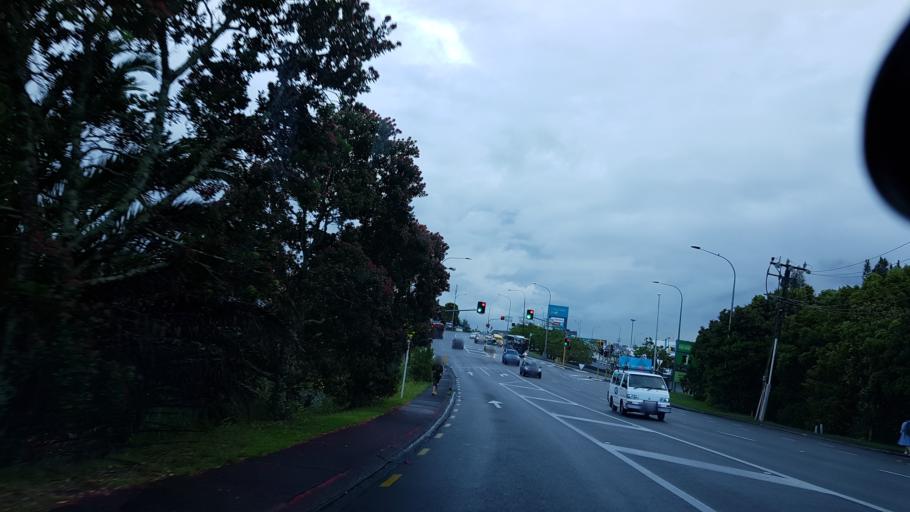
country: NZ
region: Auckland
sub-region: Auckland
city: North Shore
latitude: -36.7844
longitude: 174.7218
